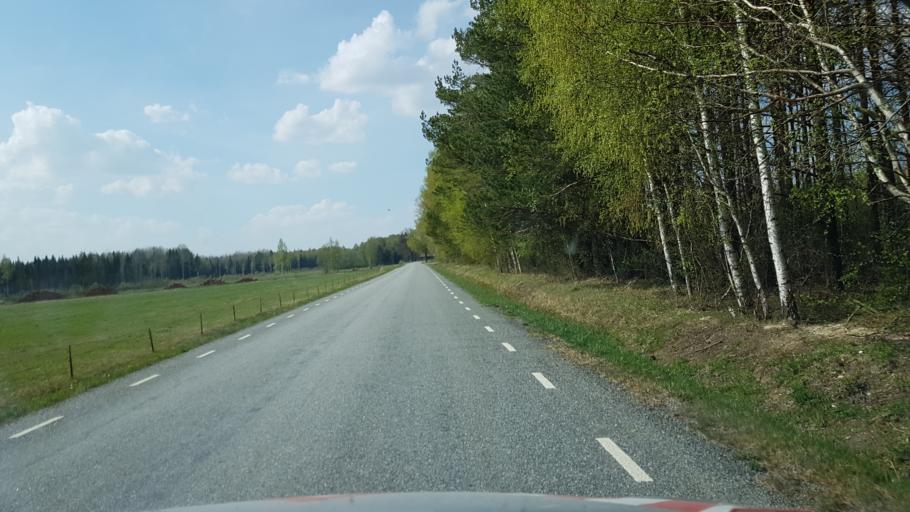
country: EE
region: Paernumaa
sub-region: Paikuse vald
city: Paikuse
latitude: 58.4369
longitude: 24.6153
